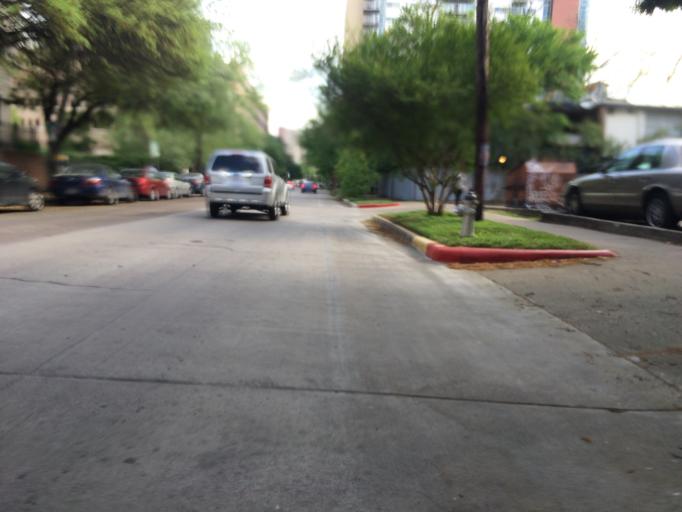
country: US
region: Texas
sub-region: Travis County
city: Austin
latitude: 30.2900
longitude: -97.7430
